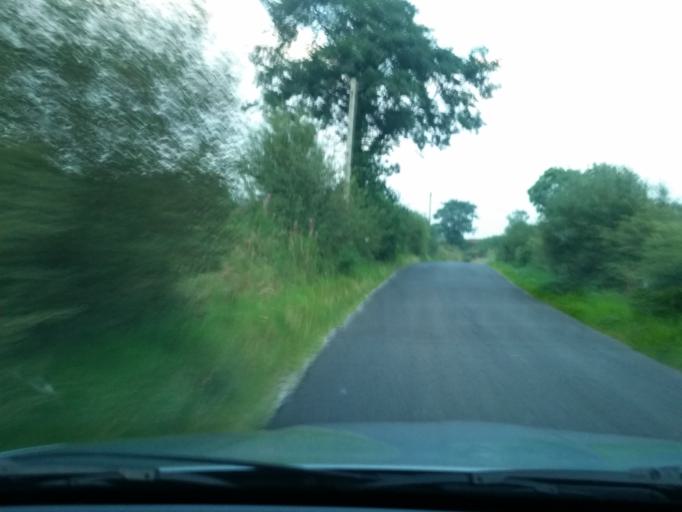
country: GB
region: Northern Ireland
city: Fivemiletown
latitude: 54.2883
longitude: -7.2788
